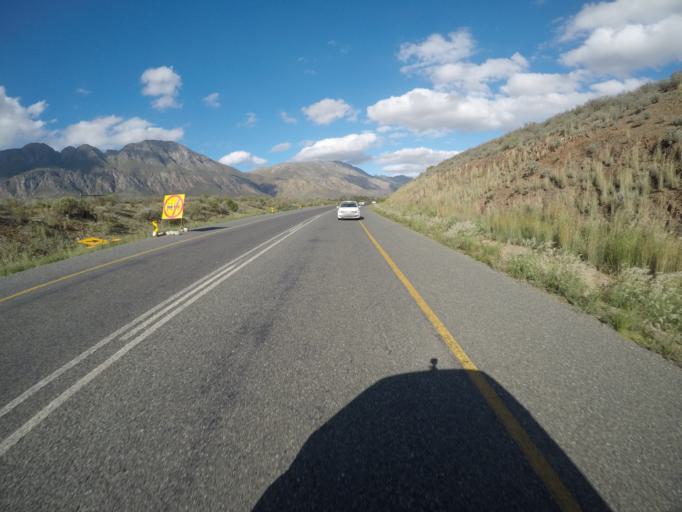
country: ZA
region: Western Cape
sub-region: Cape Winelands District Municipality
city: Ashton
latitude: -33.8659
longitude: 20.1266
